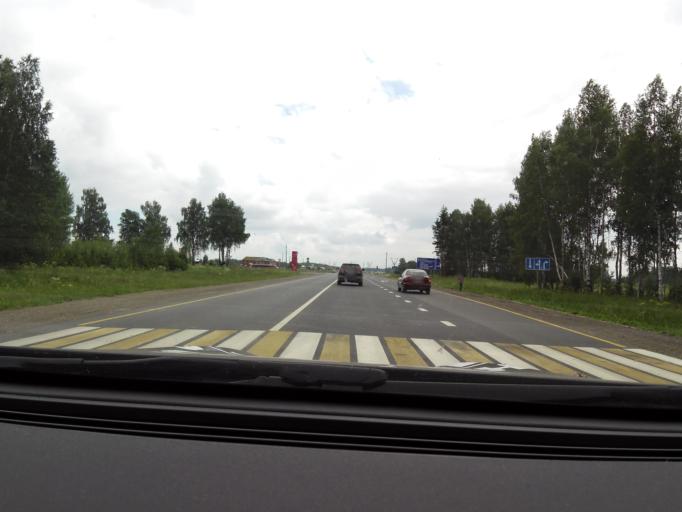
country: RU
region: Perm
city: Orda
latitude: 57.2680
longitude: 57.0169
